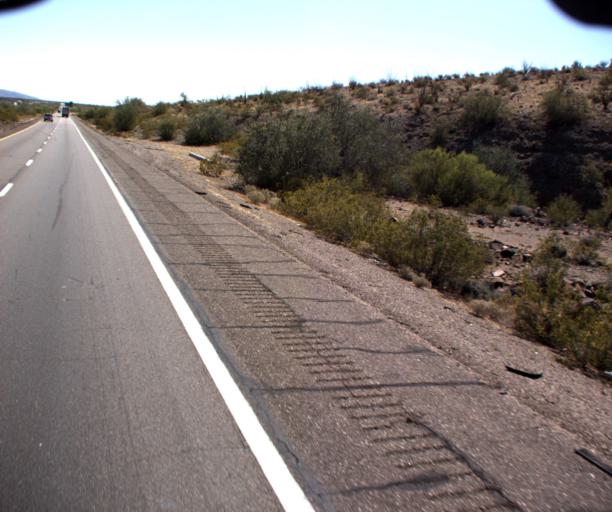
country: US
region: Arizona
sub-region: La Paz County
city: Quartzsite
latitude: 33.6632
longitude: -114.0254
